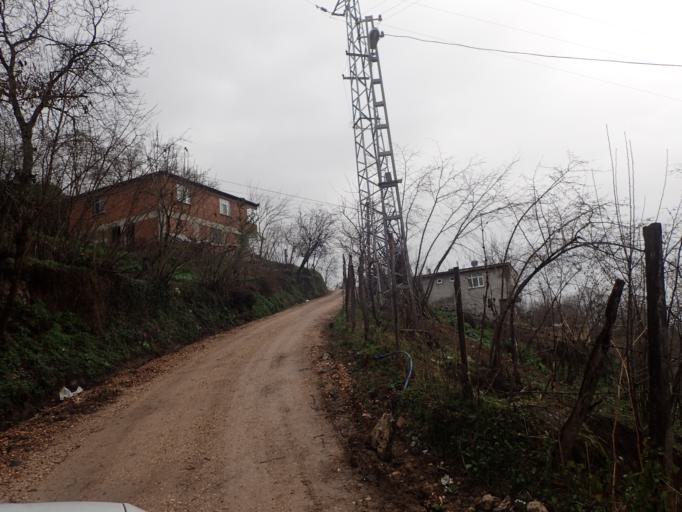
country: TR
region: Ordu
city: Camas
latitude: 40.9288
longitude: 37.5079
